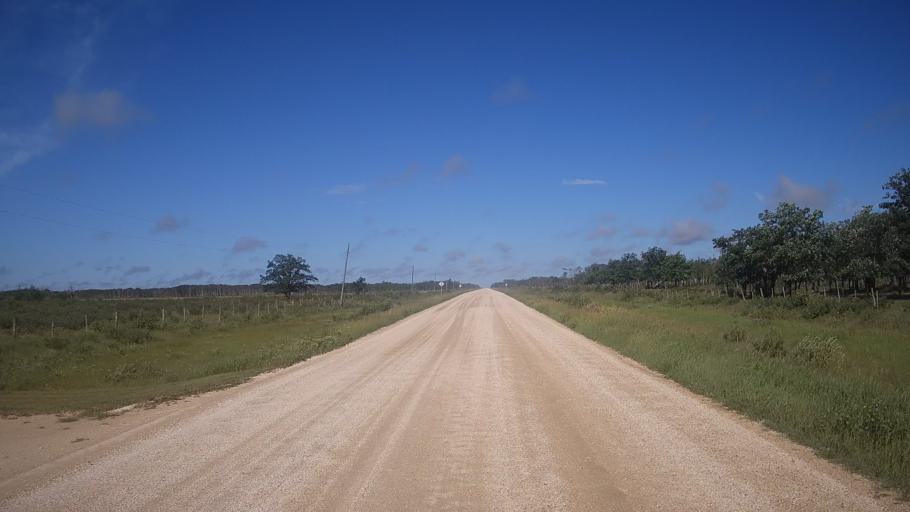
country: CA
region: Manitoba
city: Stonewall
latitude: 50.2411
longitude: -97.7376
